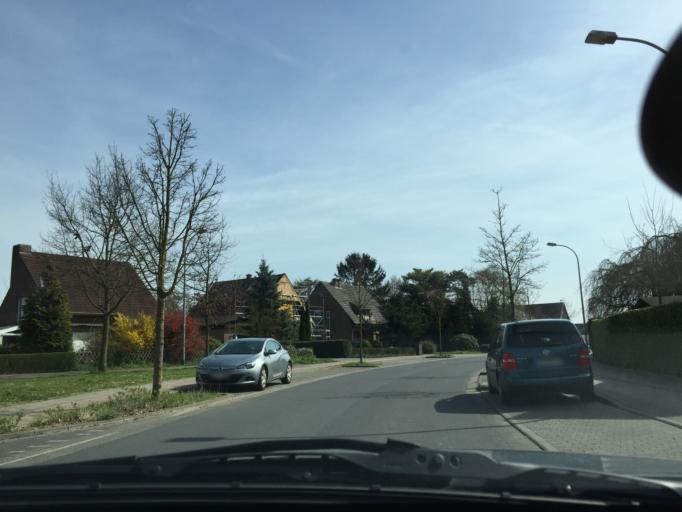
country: DE
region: North Rhine-Westphalia
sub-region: Regierungsbezirk Dusseldorf
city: Goch
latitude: 51.6674
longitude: 6.1595
